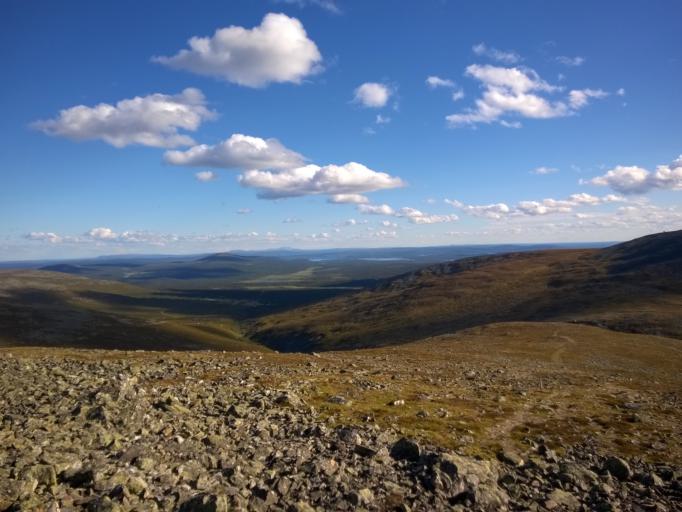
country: FI
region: Lapland
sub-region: Tunturi-Lappi
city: Muonio
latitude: 68.0723
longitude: 24.0484
